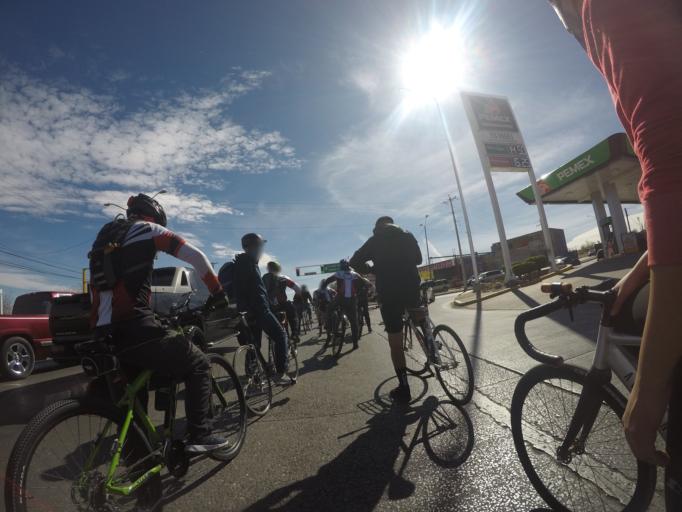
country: MX
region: Chihuahua
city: Ciudad Juarez
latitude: 31.6762
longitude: -106.4080
